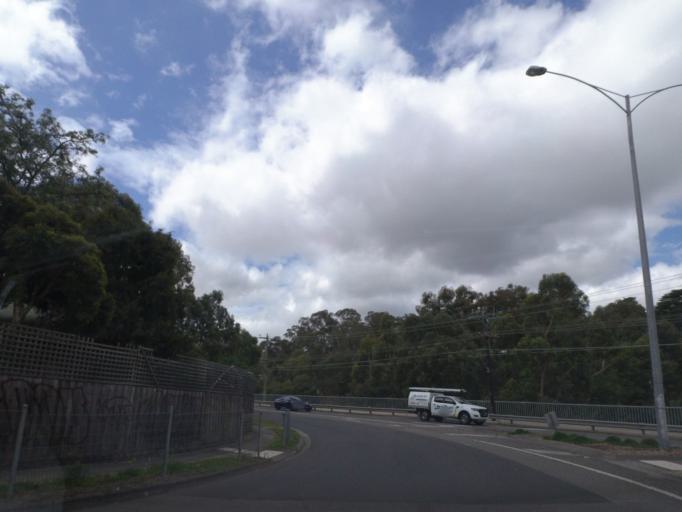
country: AU
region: Victoria
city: Saint Helena
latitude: -37.7131
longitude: 145.1334
